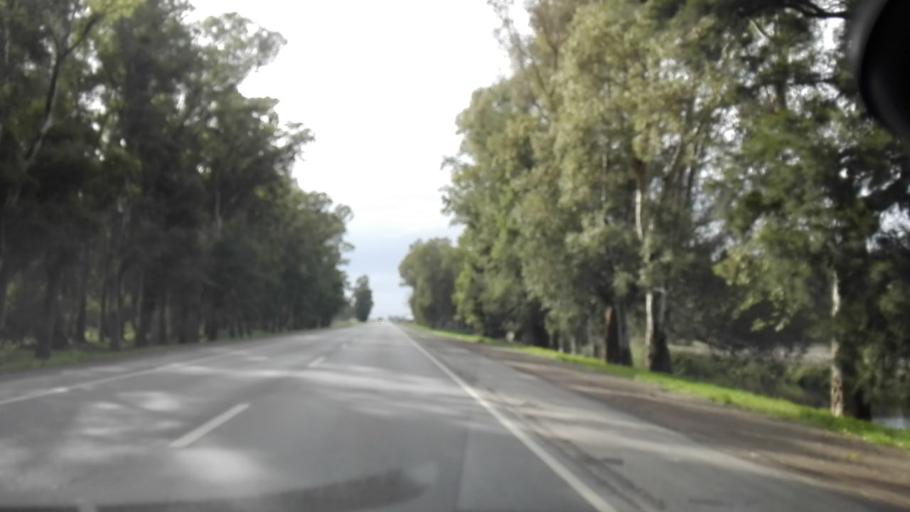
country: AR
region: Buenos Aires
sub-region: Partido de Las Flores
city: Las Flores
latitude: -36.0459
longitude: -59.0854
